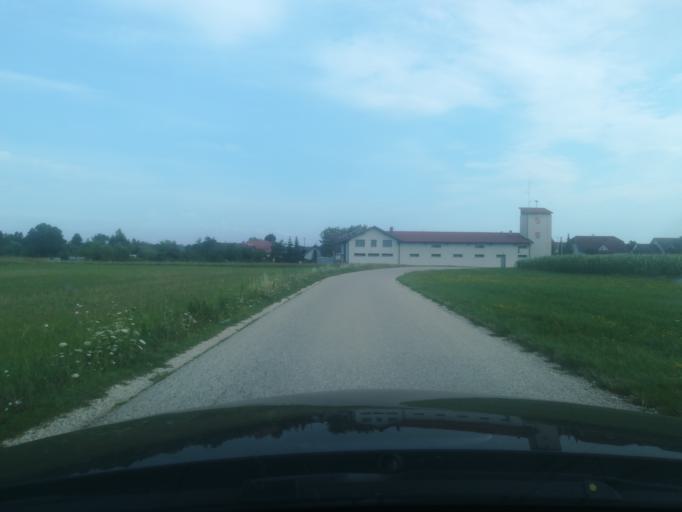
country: AT
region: Upper Austria
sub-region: Wels-Land
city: Marchtrenk
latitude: 48.1907
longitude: 14.1295
